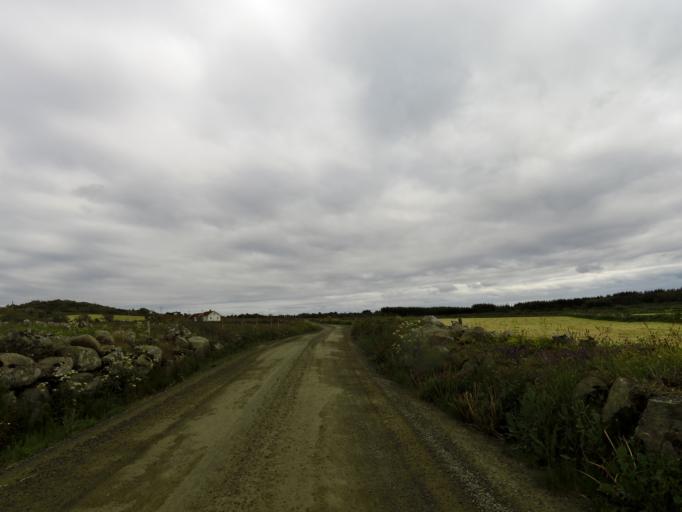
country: NO
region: Vest-Agder
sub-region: Farsund
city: Vestbygd
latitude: 58.1350
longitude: 6.6073
